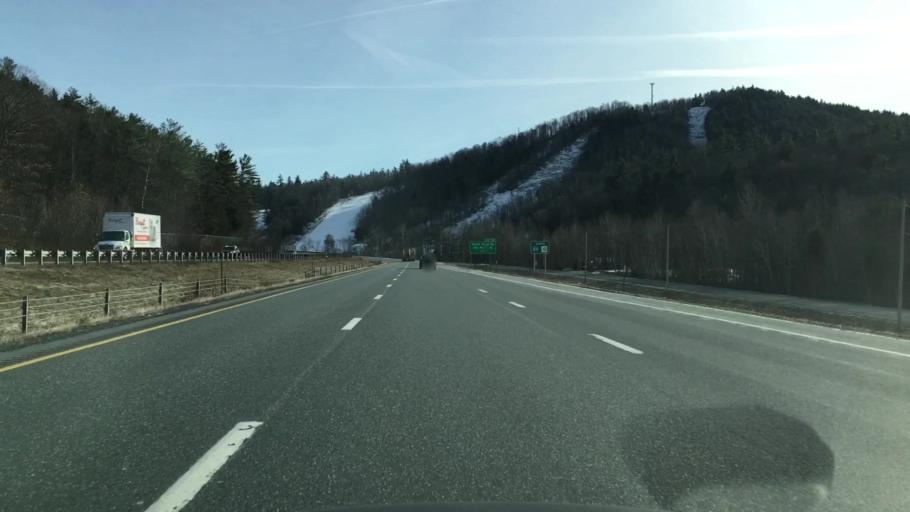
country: US
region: New Hampshire
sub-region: Grafton County
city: Enfield
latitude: 43.6064
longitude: -72.1856
